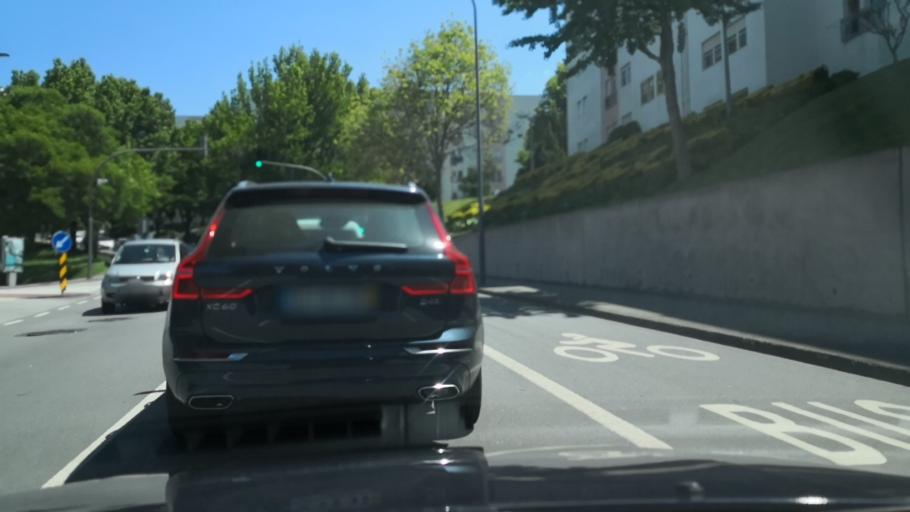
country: PT
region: Porto
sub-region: Vila Nova de Gaia
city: Canidelo
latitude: 41.1524
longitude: -8.6520
